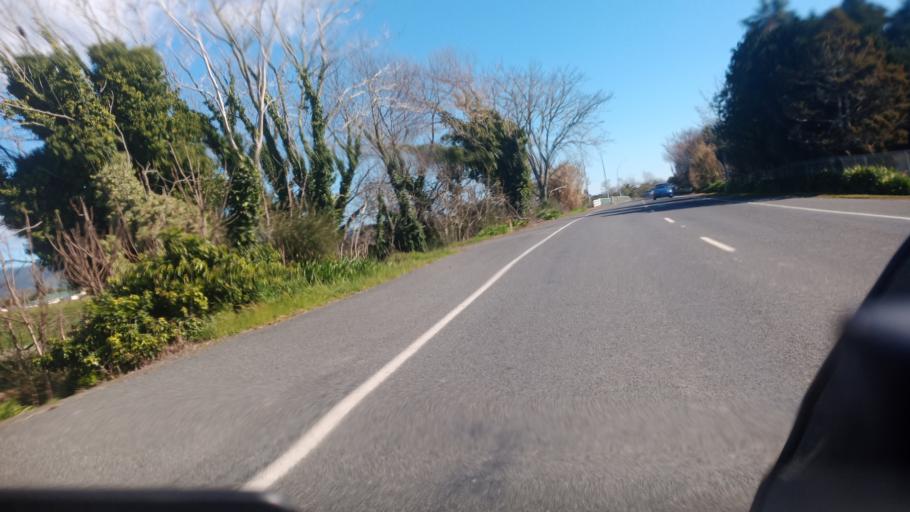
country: NZ
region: Bay of Plenty
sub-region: Opotiki District
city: Opotiki
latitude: -38.0037
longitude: 177.2931
